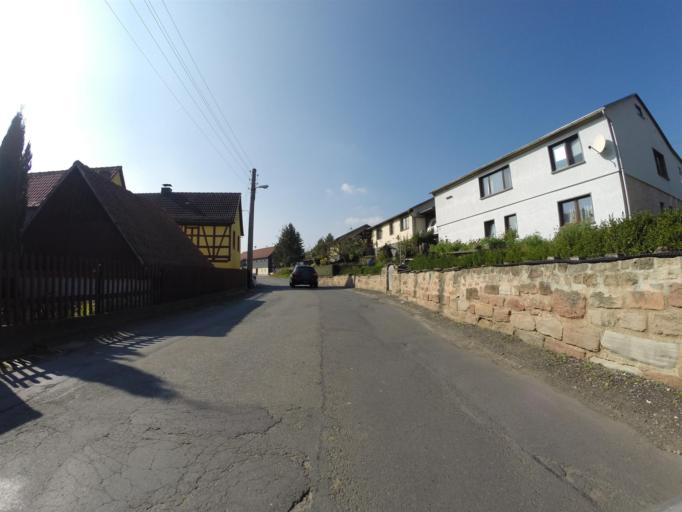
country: DE
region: Thuringia
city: Geisenhain
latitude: 50.8358
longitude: 11.7187
